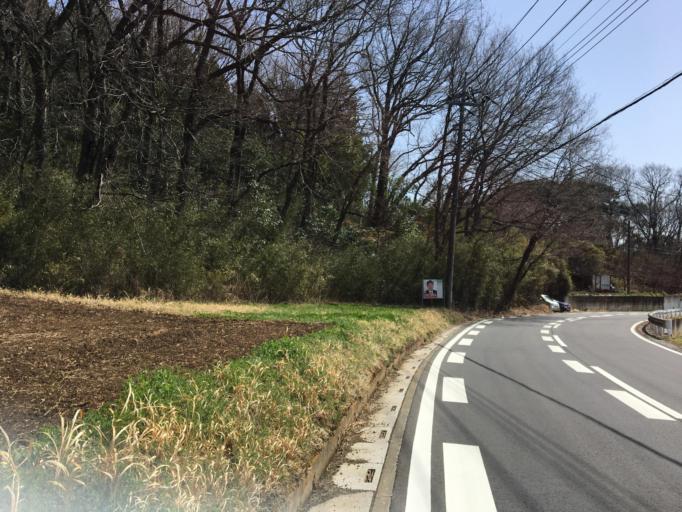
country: JP
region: Saitama
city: Sakado
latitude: 36.0023
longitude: 139.3329
